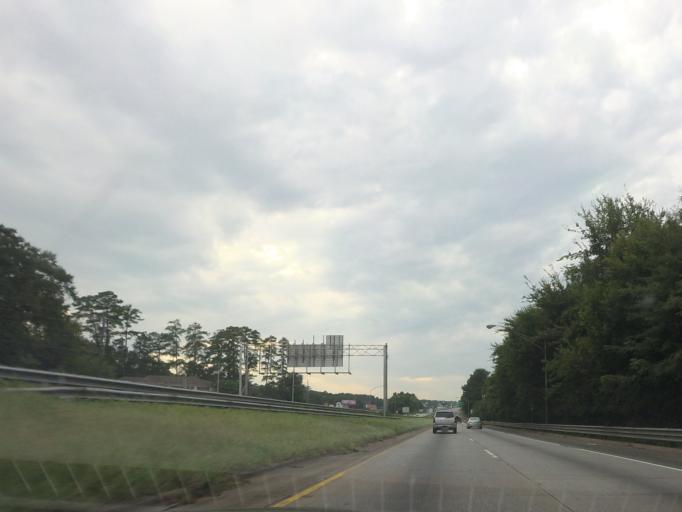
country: US
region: Georgia
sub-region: Bibb County
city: Macon
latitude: 32.8666
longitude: -83.6551
